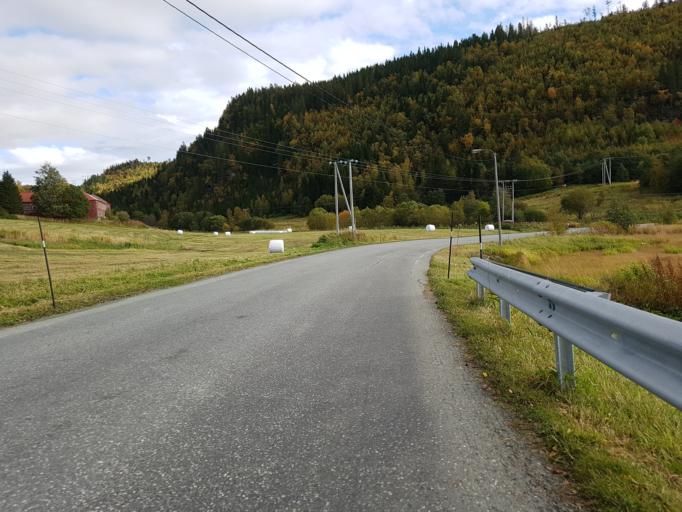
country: NO
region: Sor-Trondelag
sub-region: Klaebu
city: Klaebu
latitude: 63.3978
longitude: 10.5536
